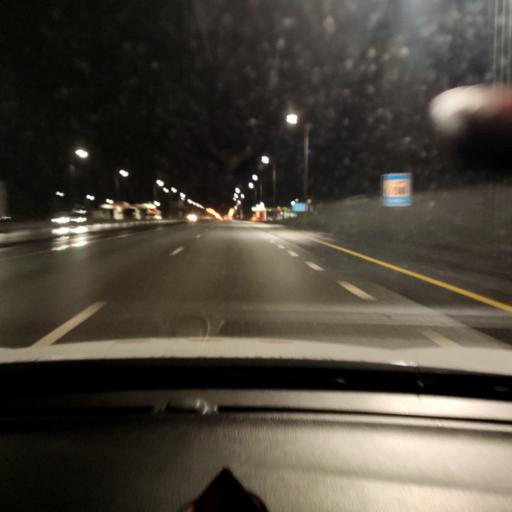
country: RU
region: Tatarstan
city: Osinovo
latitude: 55.8361
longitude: 48.8506
